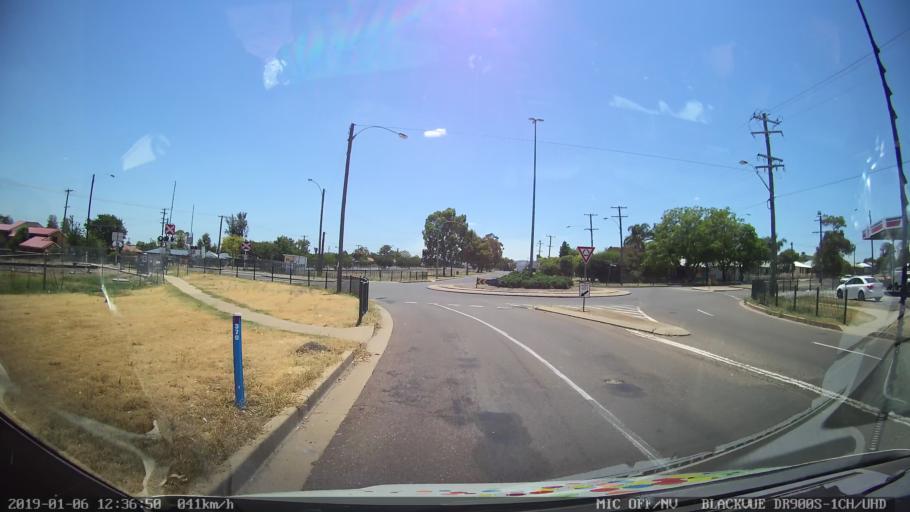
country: AU
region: New South Wales
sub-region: Tamworth Municipality
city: South Tamworth
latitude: -31.1084
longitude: 150.8990
